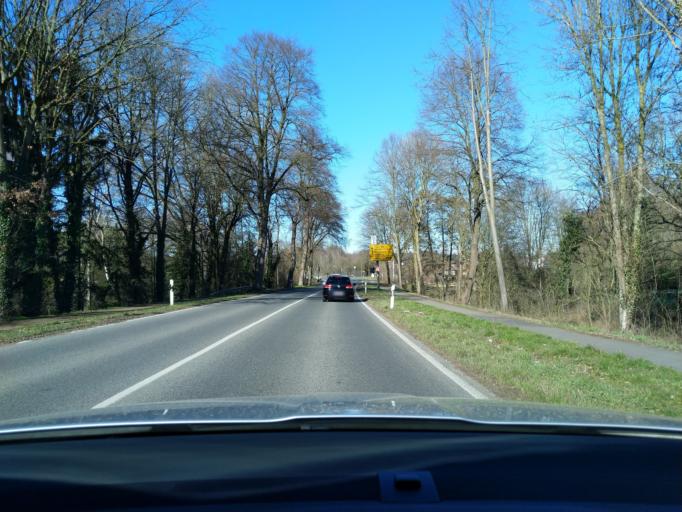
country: DE
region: North Rhine-Westphalia
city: Wegberg
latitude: 51.1372
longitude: 6.2712
